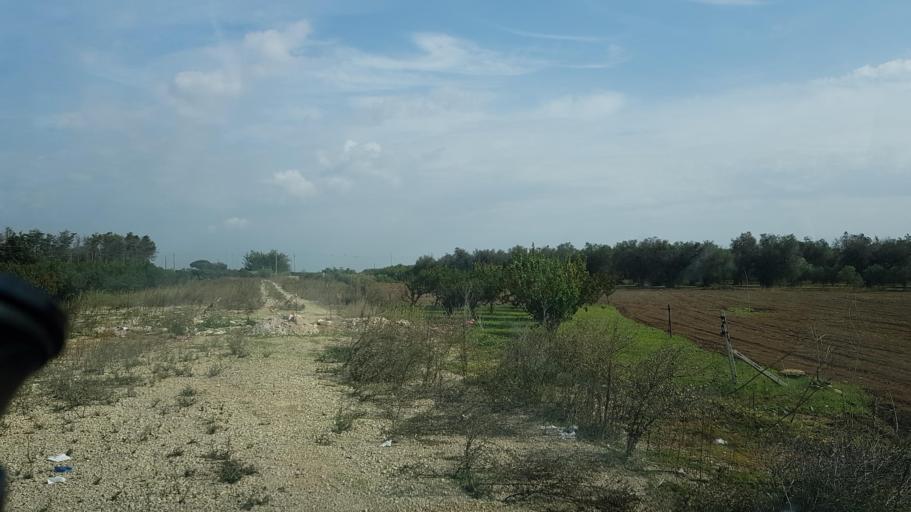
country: IT
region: Apulia
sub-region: Provincia di Brindisi
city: Mesagne
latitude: 40.5432
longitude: 17.8197
